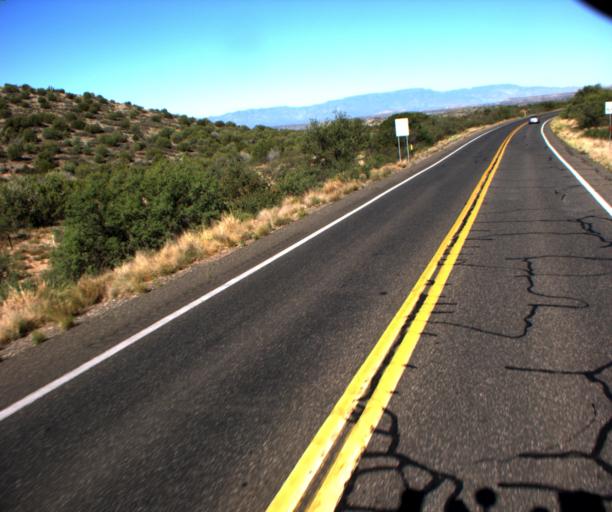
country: US
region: Arizona
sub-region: Yavapai County
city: Lake Montezuma
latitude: 34.6911
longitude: -111.7476
